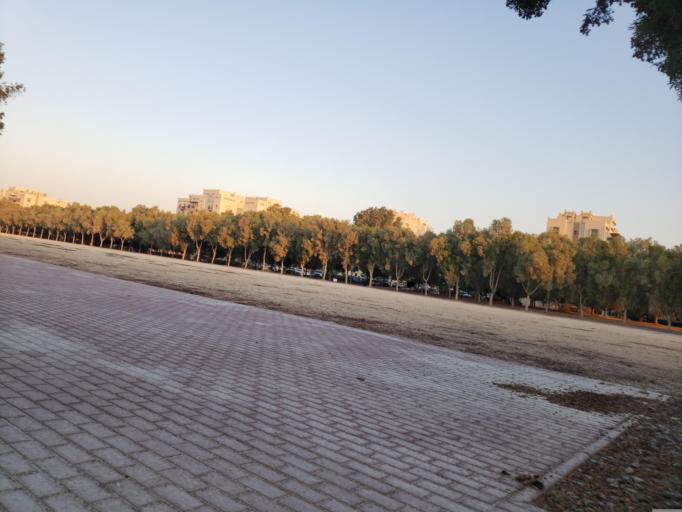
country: AE
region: Dubai
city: Dubai
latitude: 25.0063
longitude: 55.2456
